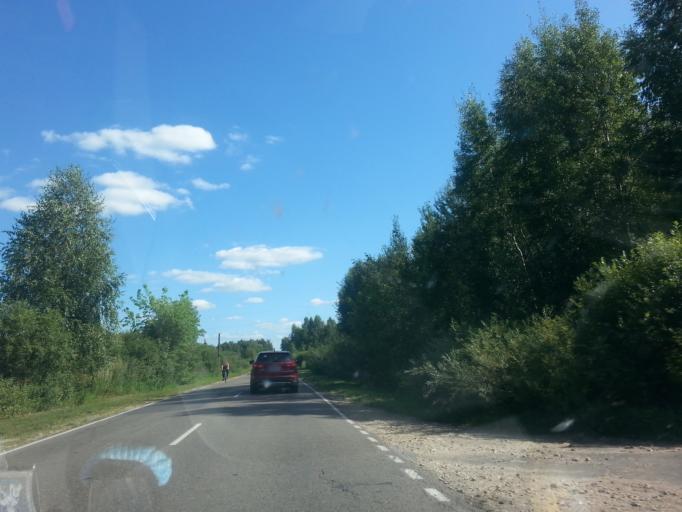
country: RU
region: Nizjnij Novgorod
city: Taremskoye
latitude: 56.0015
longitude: 42.9969
